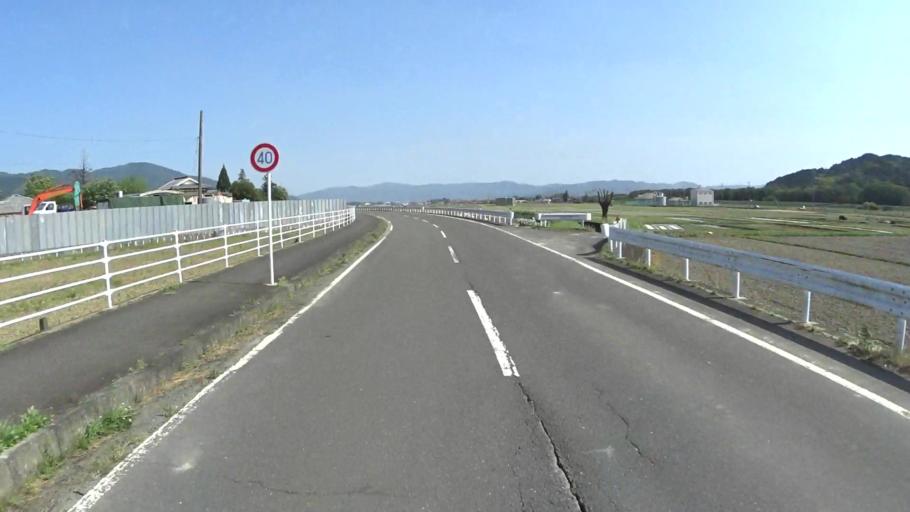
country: JP
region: Kyoto
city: Kameoka
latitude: 35.0711
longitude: 135.5464
